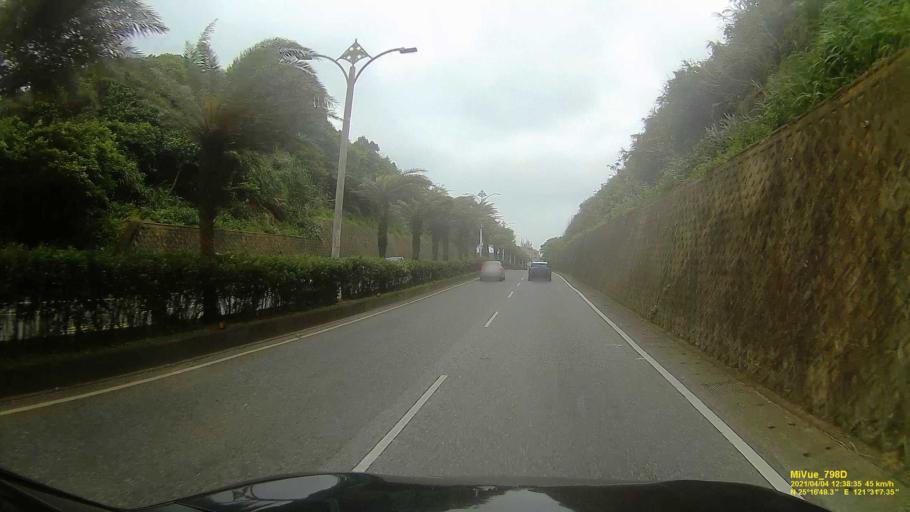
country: TW
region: Taipei
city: Taipei
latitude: 25.2801
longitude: 121.5184
